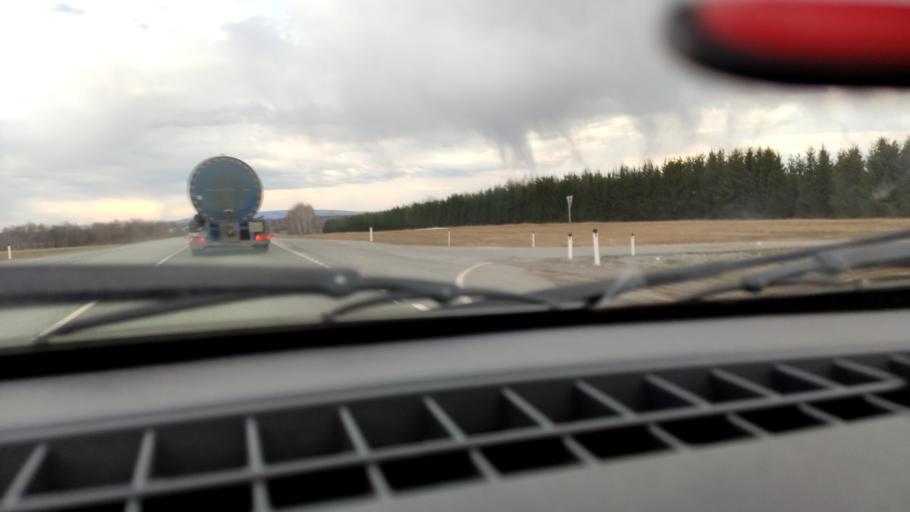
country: RU
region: Bashkortostan
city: Kudeyevskiy
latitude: 54.8167
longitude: 56.7184
